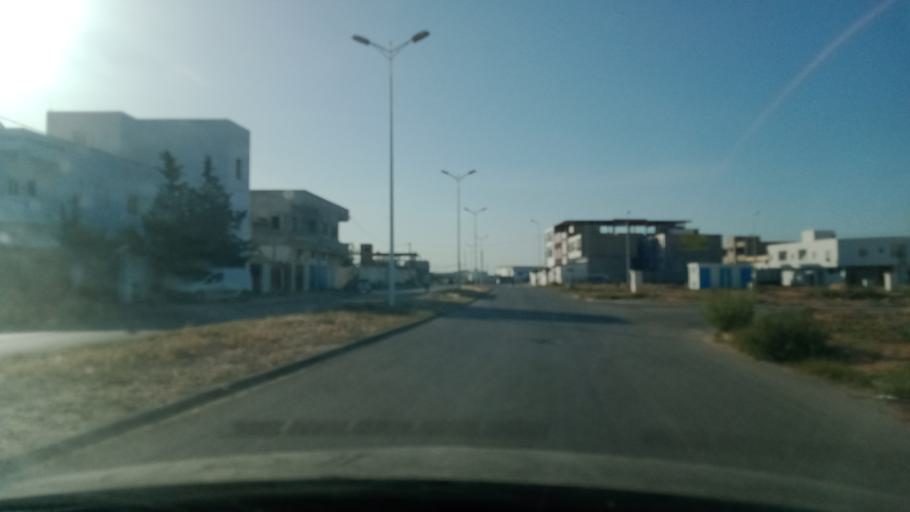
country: TN
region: Safaqis
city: Sfax
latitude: 34.8236
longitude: 10.7387
